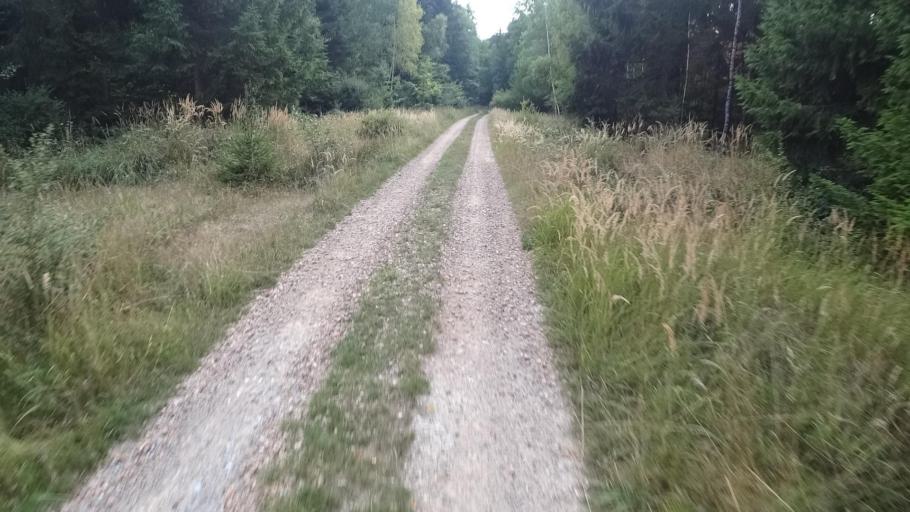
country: DE
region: Rheinland-Pfalz
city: Dichtelbach
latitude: 50.0128
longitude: 7.7123
